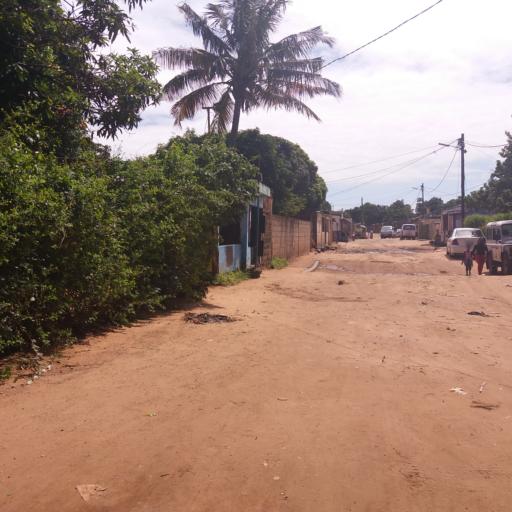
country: MZ
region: Maputo City
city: Maputo
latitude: -25.9108
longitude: 32.5904
